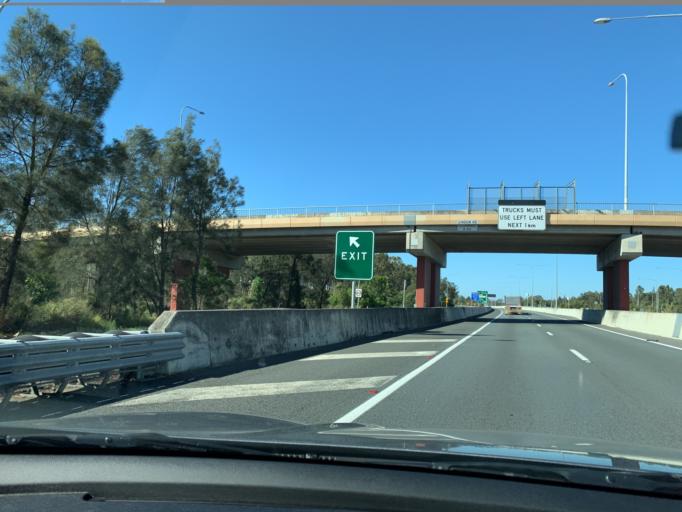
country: AU
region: Queensland
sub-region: Brisbane
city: Wynnum
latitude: -27.4405
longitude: 153.1370
